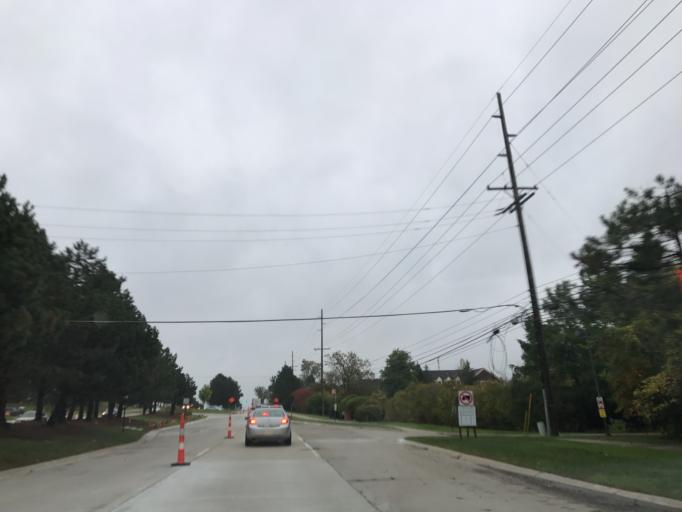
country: US
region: Michigan
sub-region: Oakland County
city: Farmington Hills
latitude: 42.4974
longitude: -83.4241
